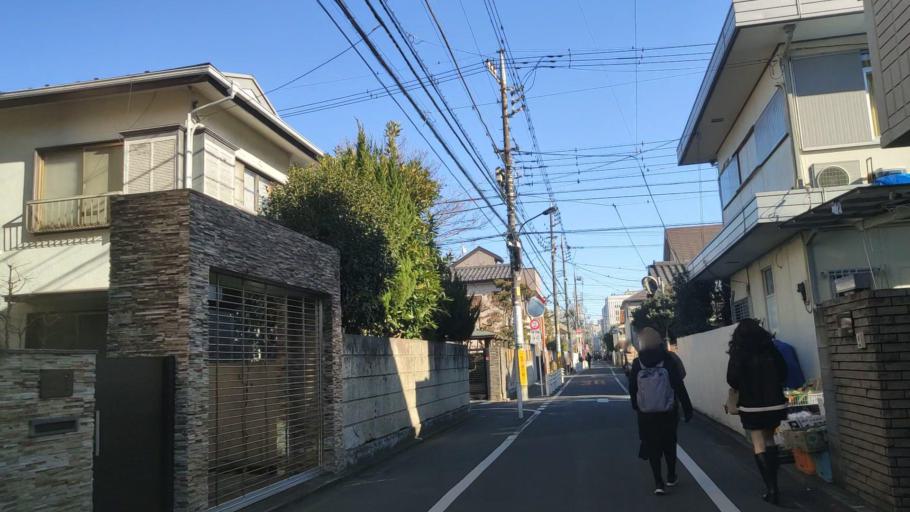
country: JP
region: Tokyo
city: Musashino
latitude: 35.7072
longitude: 139.5733
